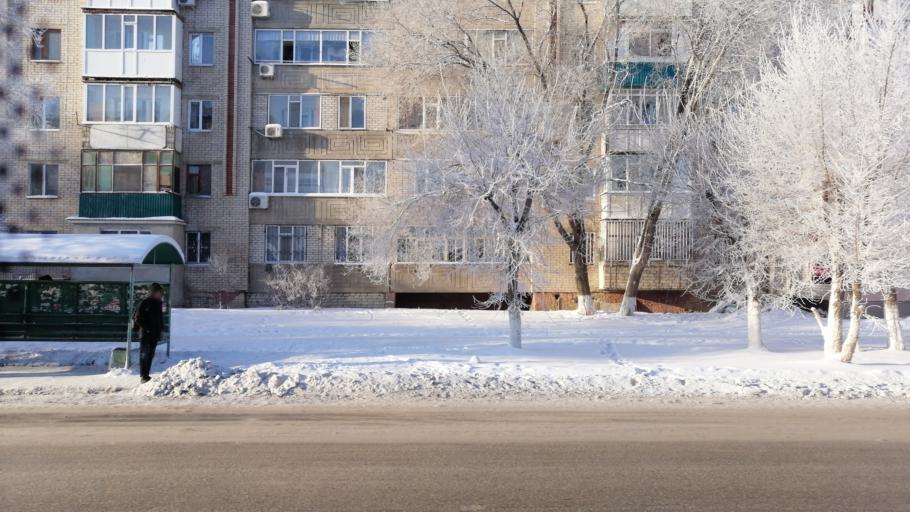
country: KZ
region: Aqtoebe
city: Aqtobe
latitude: 50.2962
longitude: 57.1467
